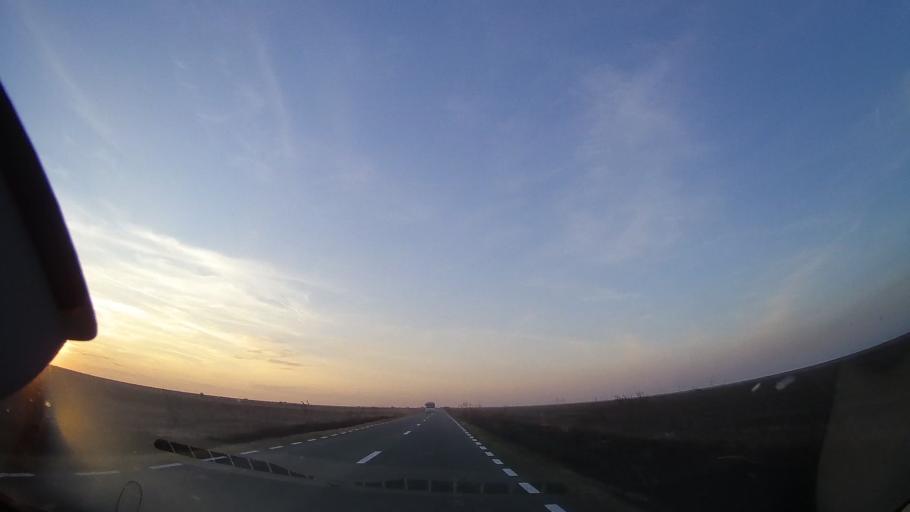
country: RO
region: Constanta
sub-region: Comuna Topraisar
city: Topraisar
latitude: 44.0191
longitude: 28.4231
